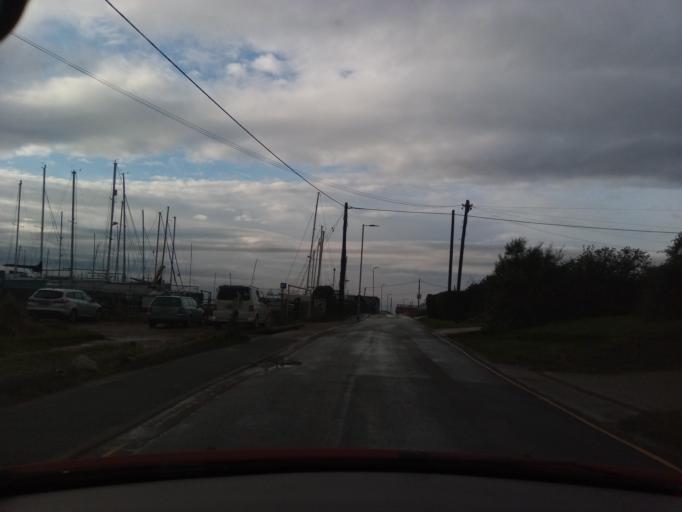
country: GB
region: England
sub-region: Essex
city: West Mersea
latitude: 51.7760
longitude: 0.9017
